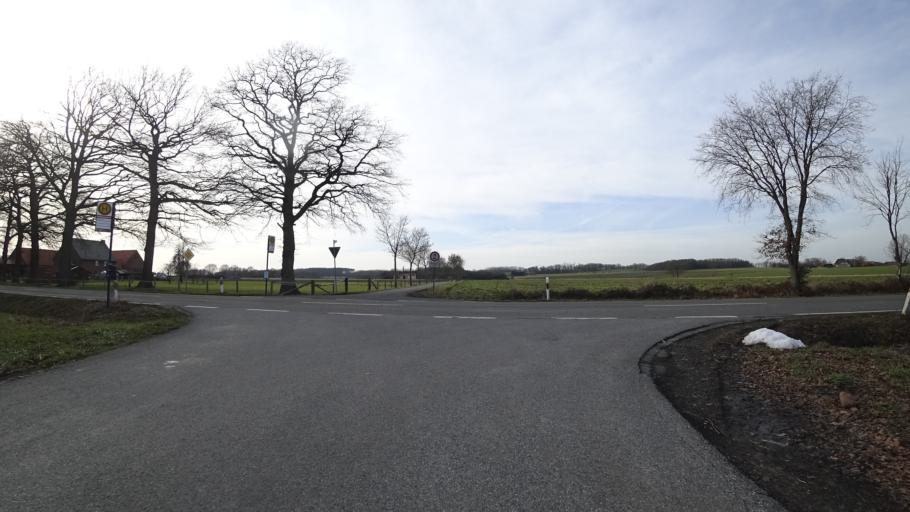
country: DE
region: North Rhine-Westphalia
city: Oelde
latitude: 51.8102
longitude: 8.1025
